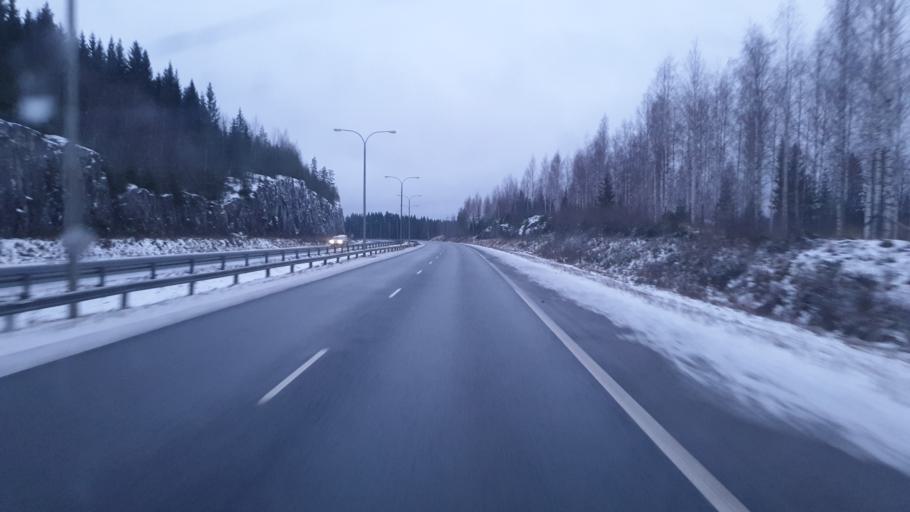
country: FI
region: Northern Savo
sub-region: Kuopio
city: Siilinjaervi
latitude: 63.0383
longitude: 27.6594
